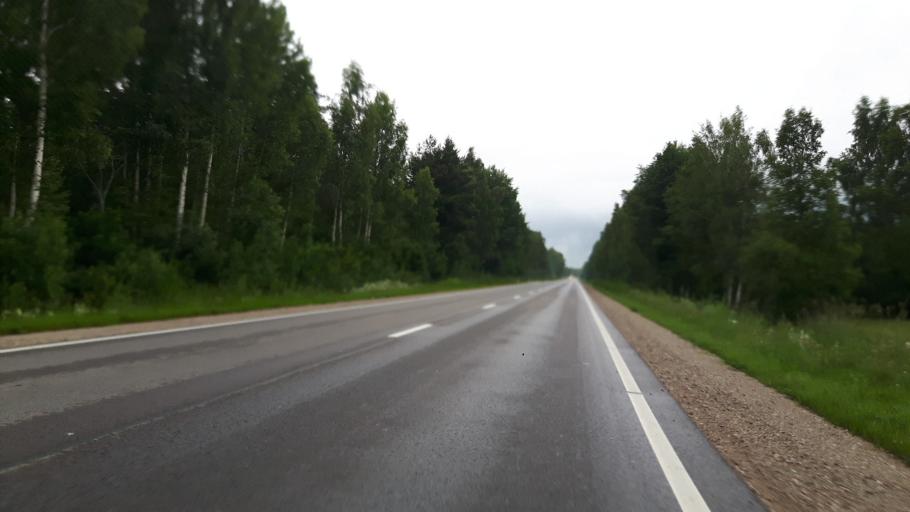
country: LV
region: Rucavas
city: Rucava
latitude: 56.2362
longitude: 21.1068
